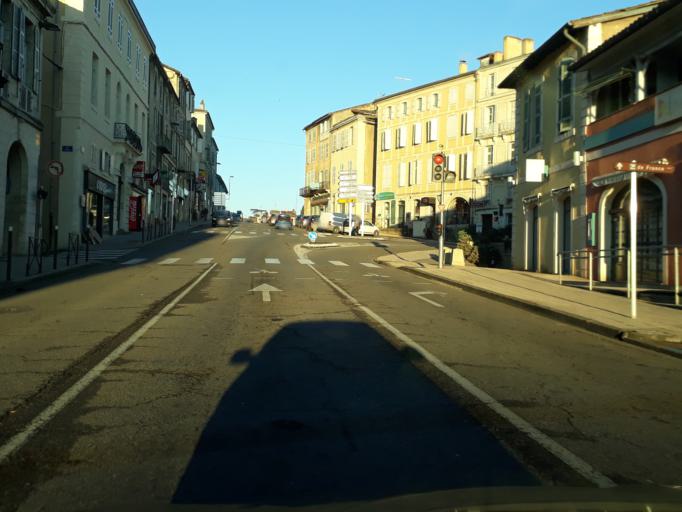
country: FR
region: Midi-Pyrenees
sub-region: Departement du Gers
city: Auch
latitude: 43.6492
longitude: 0.5887
